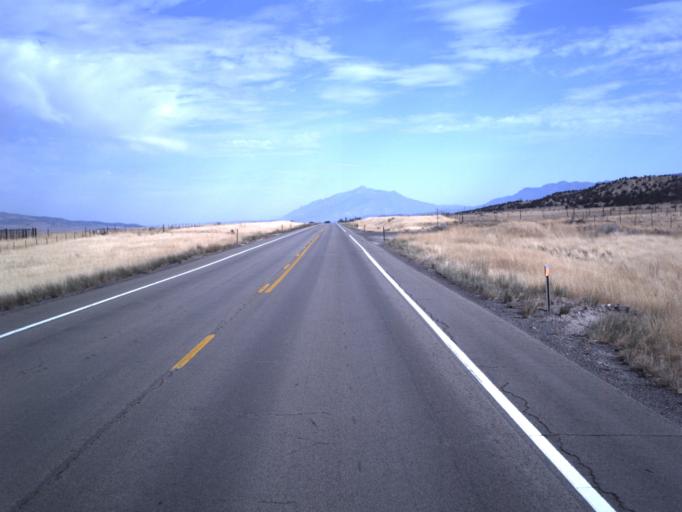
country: US
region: Utah
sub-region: Sanpete County
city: Gunnison
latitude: 39.4209
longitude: -111.9219
